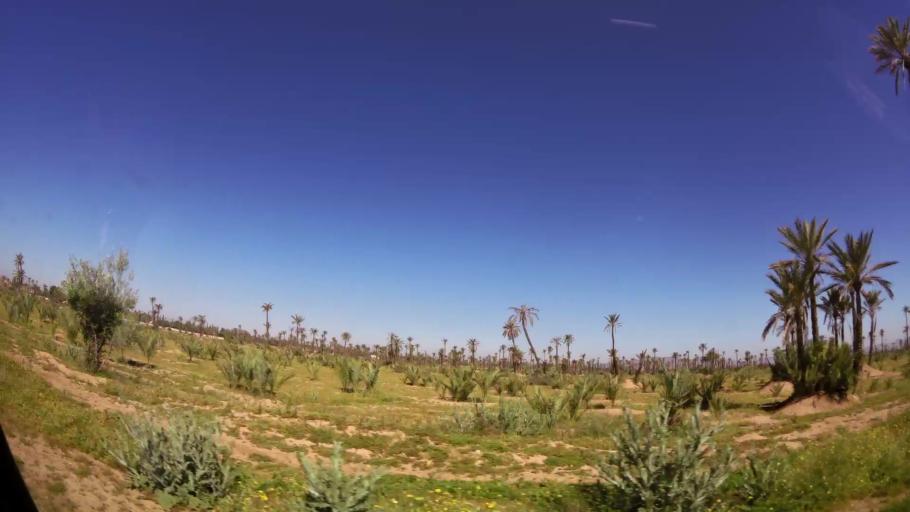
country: MA
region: Marrakech-Tensift-Al Haouz
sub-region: Marrakech
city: Marrakesh
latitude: 31.6591
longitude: -7.9494
